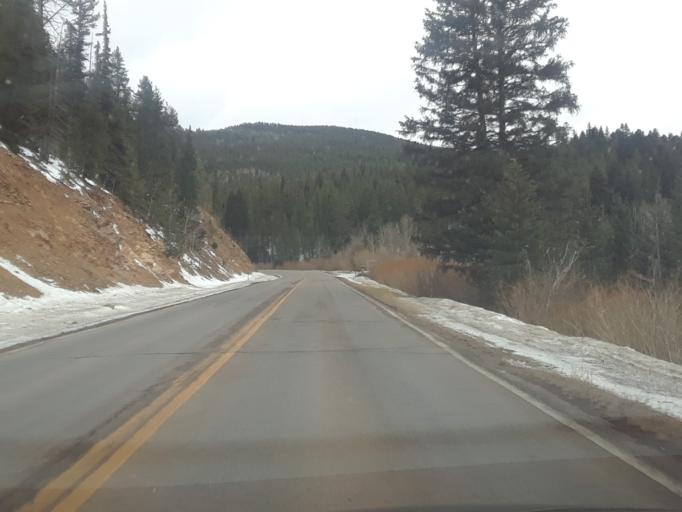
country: US
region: Colorado
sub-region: Boulder County
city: Coal Creek
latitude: 39.8268
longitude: -105.4102
